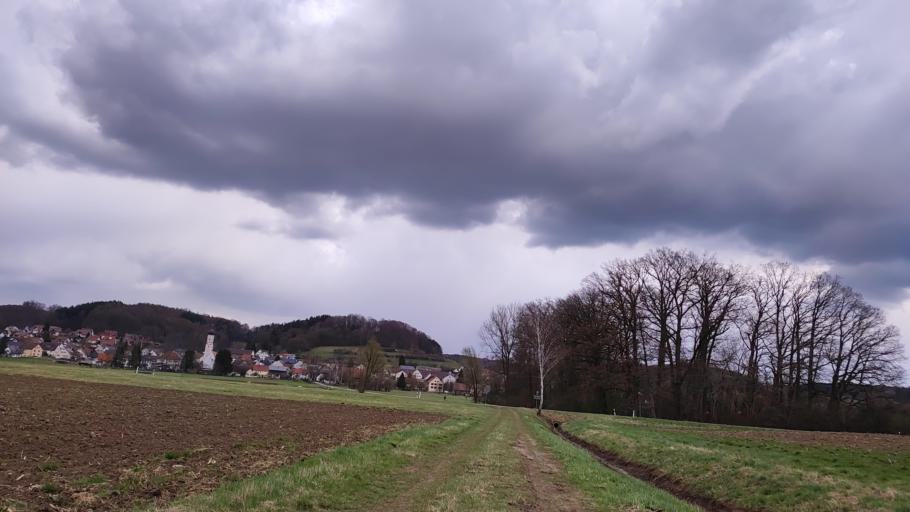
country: DE
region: Bavaria
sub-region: Swabia
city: Dinkelscherben
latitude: 48.3720
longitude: 10.5698
